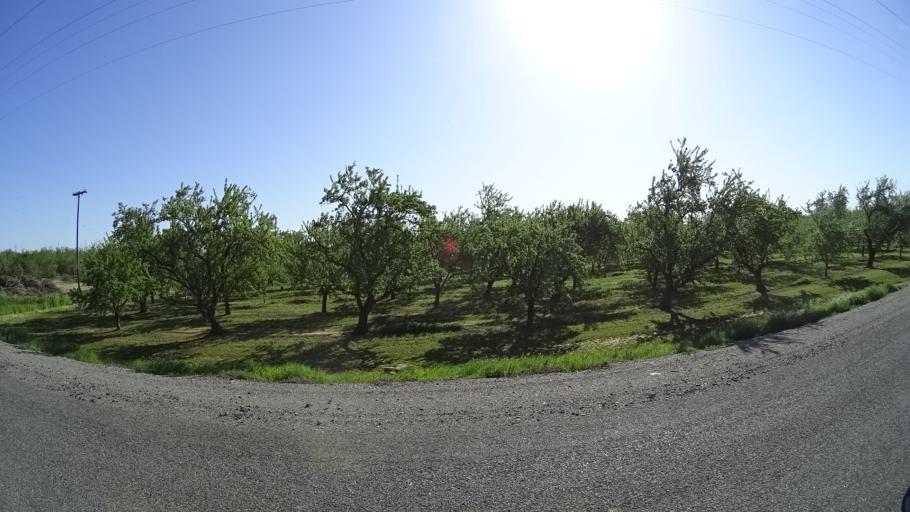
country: US
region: California
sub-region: Glenn County
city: Hamilton City
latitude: 39.7734
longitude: -122.0854
